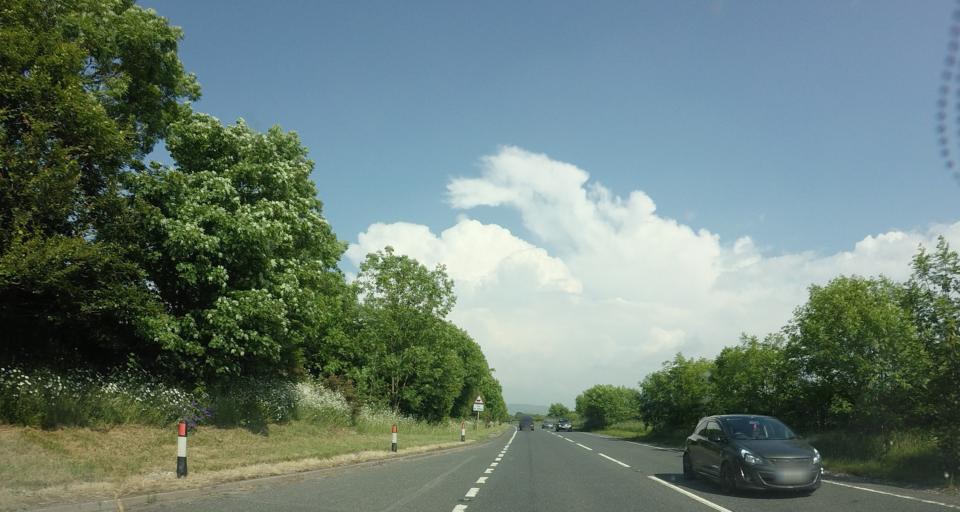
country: GB
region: England
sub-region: Cumbria
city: Cockermouth
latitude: 54.6503
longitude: -3.3534
